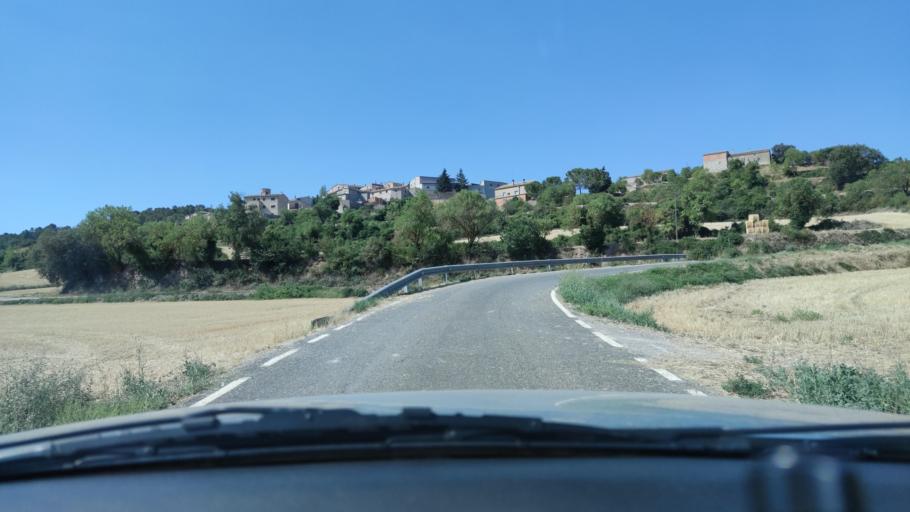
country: ES
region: Catalonia
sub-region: Provincia de Lleida
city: Sant Guim de Freixenet
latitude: 41.6642
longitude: 1.3689
